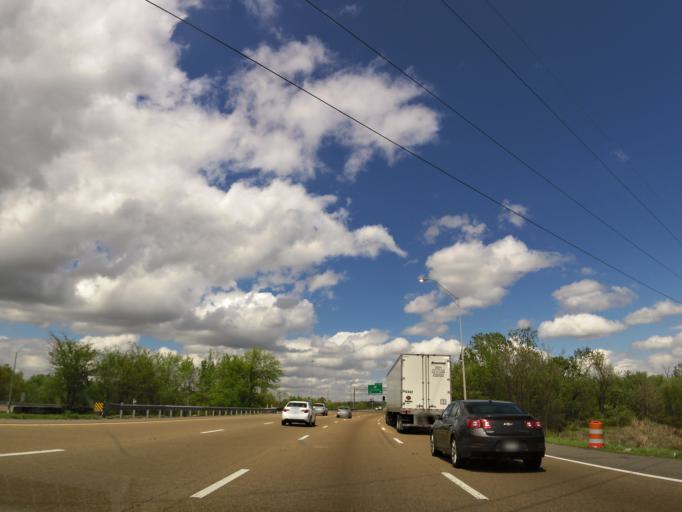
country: US
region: Tennessee
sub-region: Shelby County
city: Memphis
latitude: 35.1853
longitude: -90.0175
